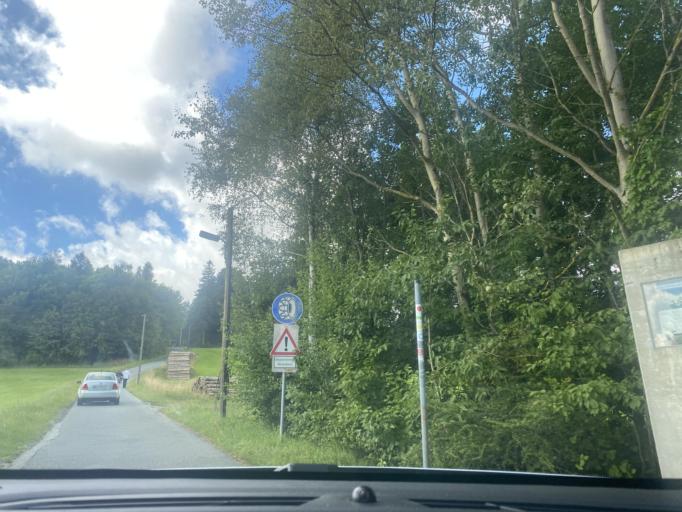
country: DE
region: Saxony
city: Beiersdorf
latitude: 51.0810
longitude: 14.5266
